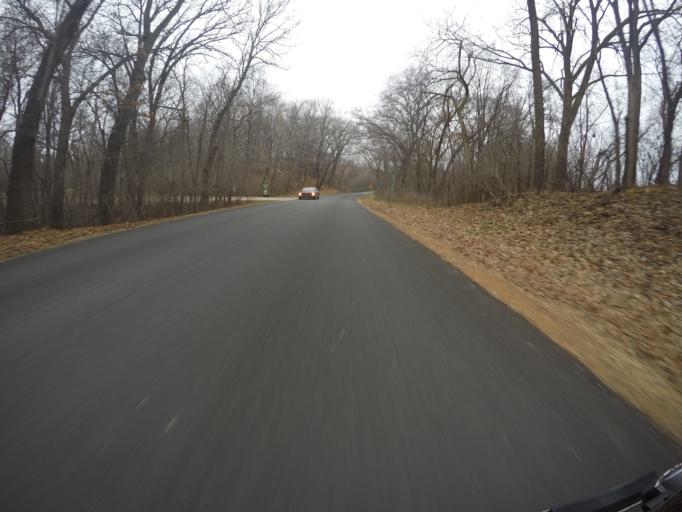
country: US
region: Minnesota
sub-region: Hennepin County
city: Eden Prairie
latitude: 44.8868
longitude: -93.4607
